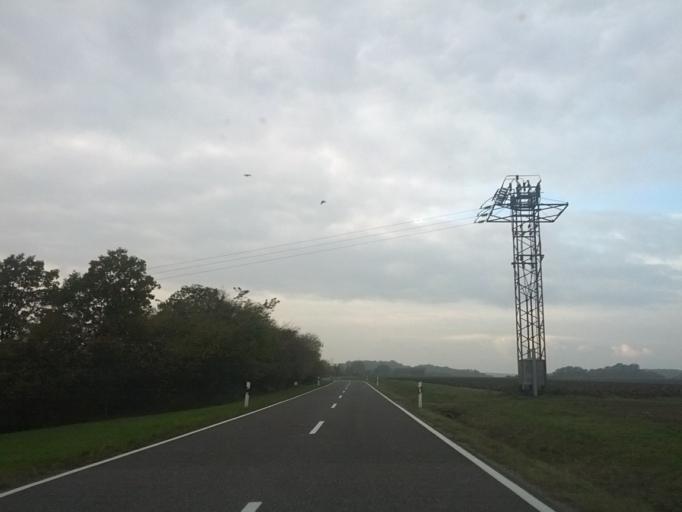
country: DE
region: Hesse
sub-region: Regierungsbezirk Kassel
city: Herleshausen
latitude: 51.0410
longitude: 10.1557
